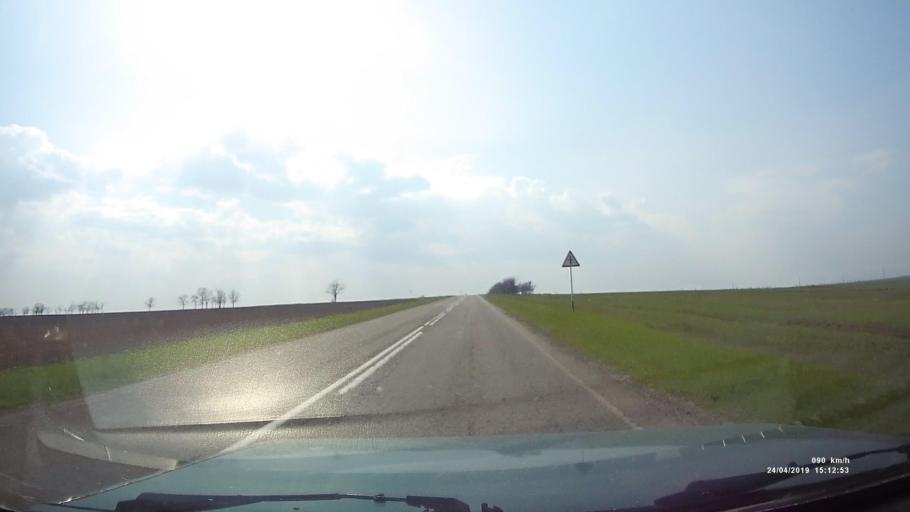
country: RU
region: Rostov
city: Remontnoye
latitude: 46.5464
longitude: 43.2911
